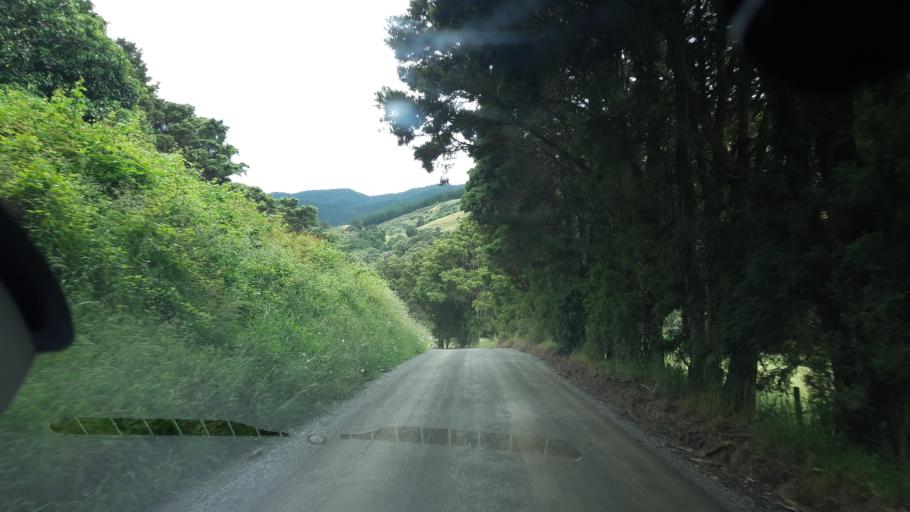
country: NZ
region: Tasman
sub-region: Tasman District
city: Brightwater
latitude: -41.4380
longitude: 173.1074
